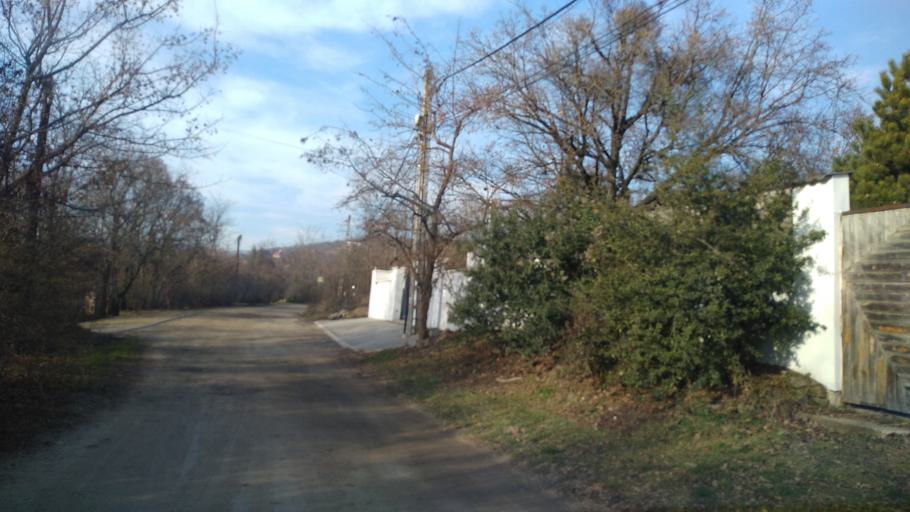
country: HU
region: Pest
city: Szentendre
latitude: 47.6979
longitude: 19.0546
